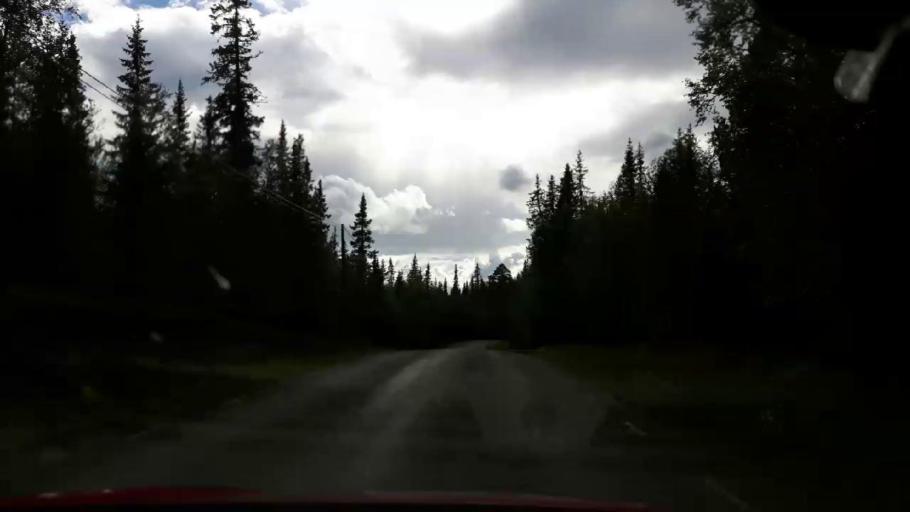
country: SE
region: Jaemtland
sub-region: Are Kommun
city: Are
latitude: 63.1577
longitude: 13.0409
